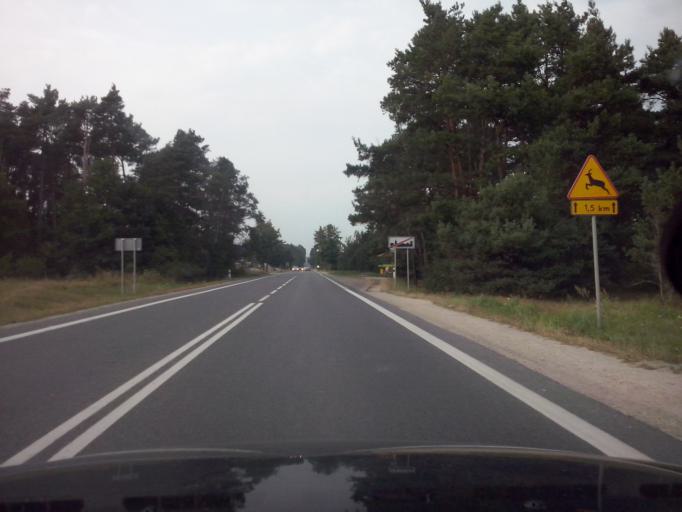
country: PL
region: Swietokrzyskie
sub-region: Powiat kielecki
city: Morawica
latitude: 50.7573
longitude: 20.6185
